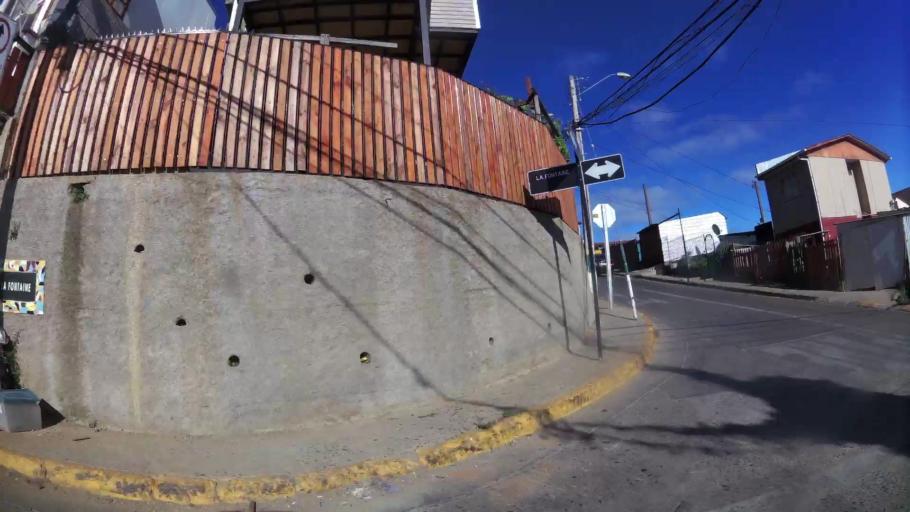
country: CL
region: Valparaiso
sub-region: Provincia de Valparaiso
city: Valparaiso
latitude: -33.0582
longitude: -71.6106
